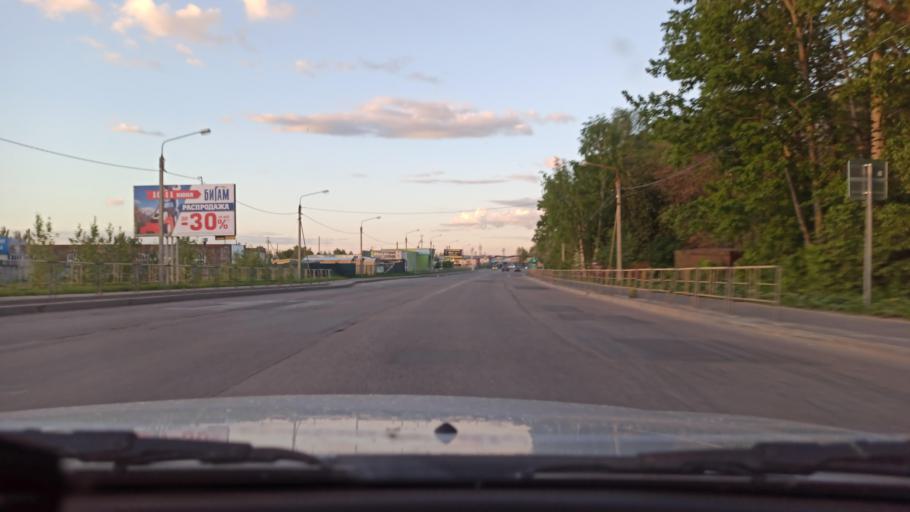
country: RU
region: Vologda
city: Vologda
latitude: 59.2196
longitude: 39.8249
